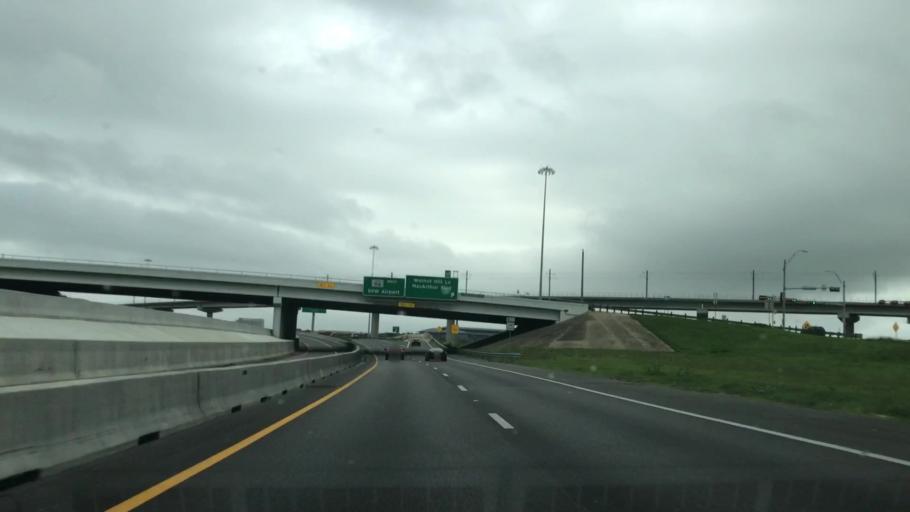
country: US
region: Texas
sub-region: Dallas County
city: Irving
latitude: 32.8788
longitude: -96.9467
